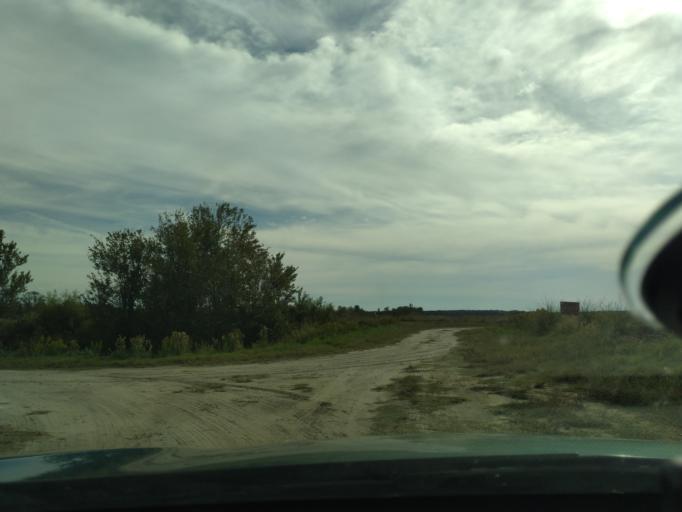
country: US
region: North Carolina
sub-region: Beaufort County
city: Belhaven
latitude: 35.7110
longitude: -76.5797
